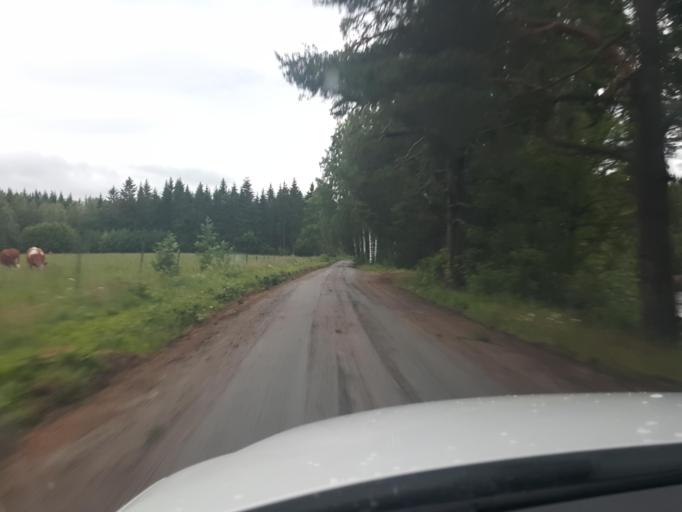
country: SE
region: Gaevleborg
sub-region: Bollnas Kommun
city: Kilafors
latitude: 61.2580
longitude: 16.6498
